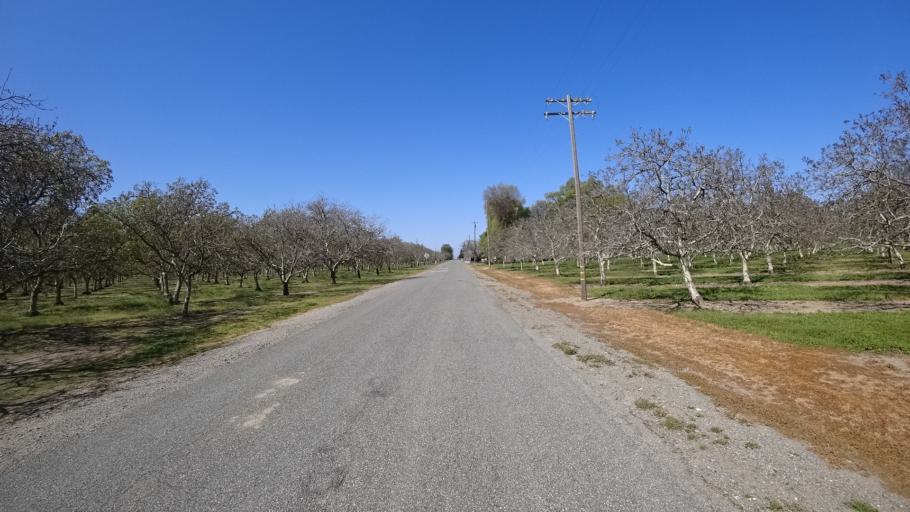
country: US
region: California
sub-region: Glenn County
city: Willows
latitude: 39.4355
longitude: -122.0120
